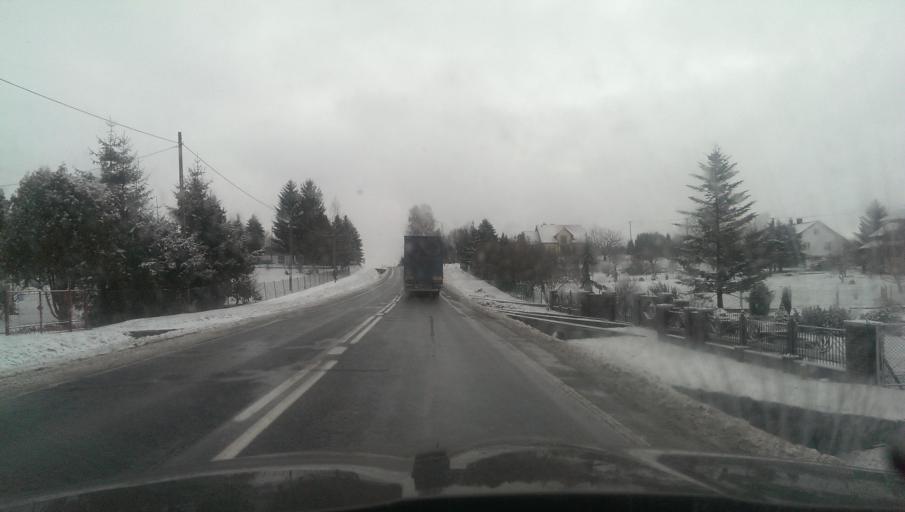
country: PL
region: Subcarpathian Voivodeship
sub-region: Powiat sanocki
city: Nowosielce-Gniewosz
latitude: 49.5627
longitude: 22.0830
